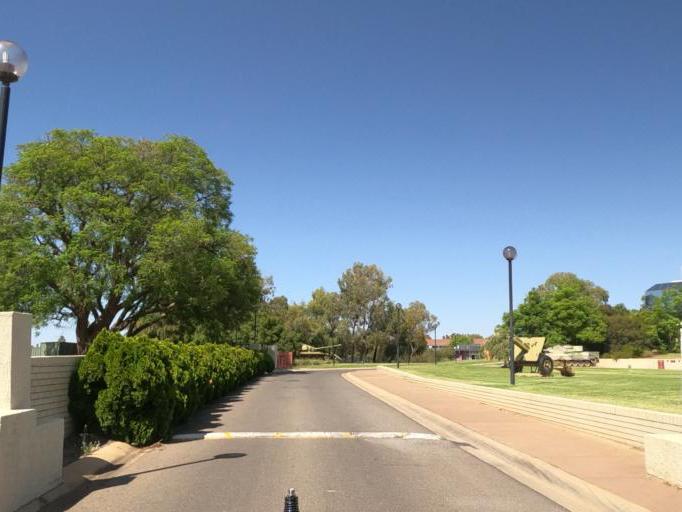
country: AU
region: New South Wales
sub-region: Corowa Shire
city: Mulwala
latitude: -36.0031
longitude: 146.0026
